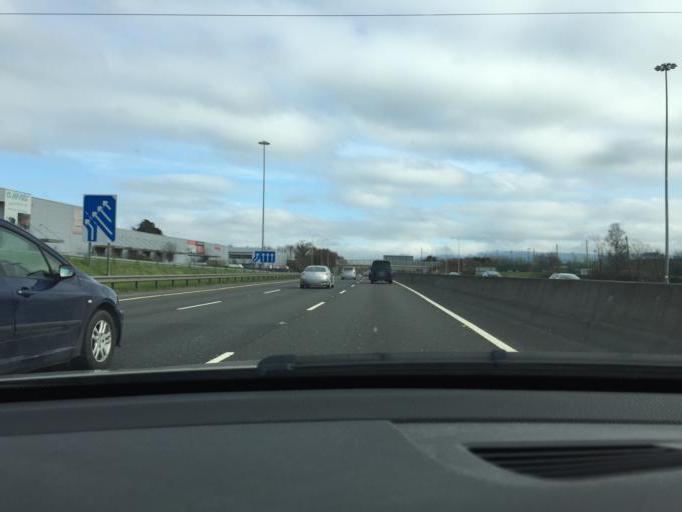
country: IE
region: Leinster
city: Tallaght
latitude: 53.3065
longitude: -6.3542
